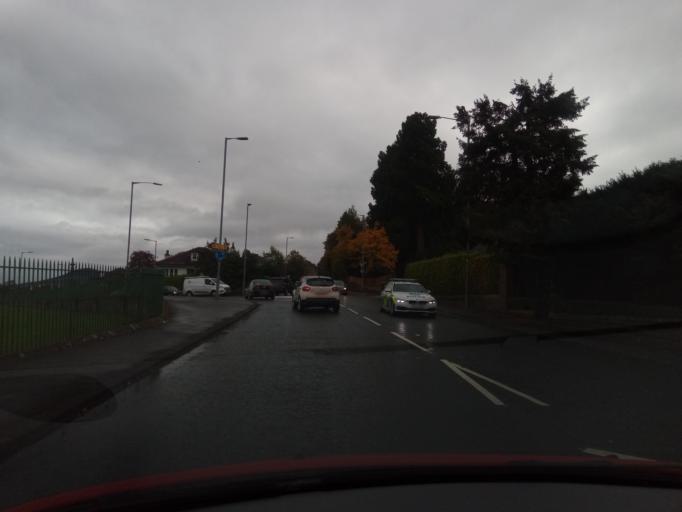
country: GB
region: Scotland
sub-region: The Scottish Borders
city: Galashiels
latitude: 55.6088
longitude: -2.7972
